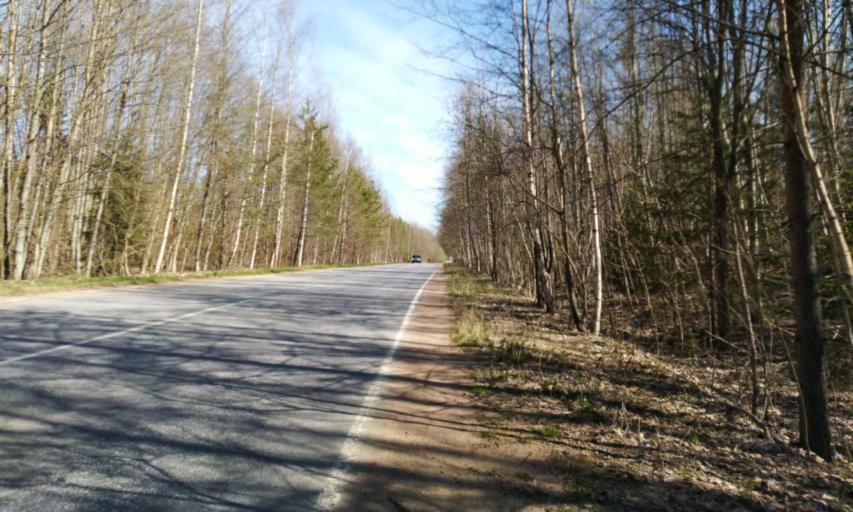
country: RU
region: Leningrad
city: Garbolovo
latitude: 60.4181
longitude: 30.4590
